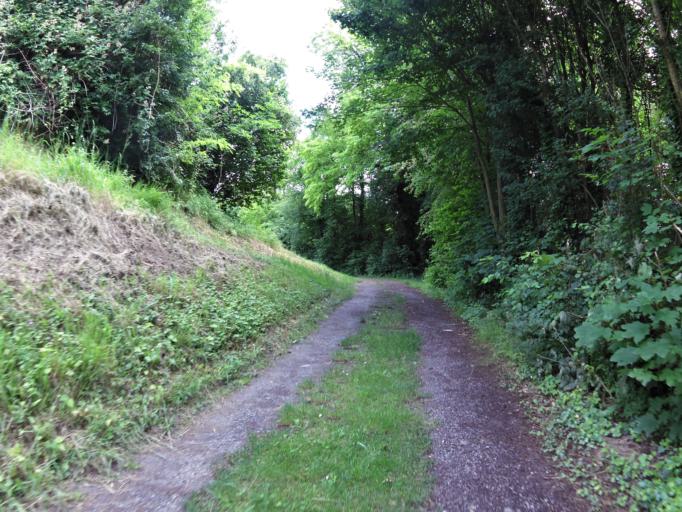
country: DE
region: Baden-Wuerttemberg
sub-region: Freiburg Region
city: Lahr
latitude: 48.3453
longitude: 7.8534
